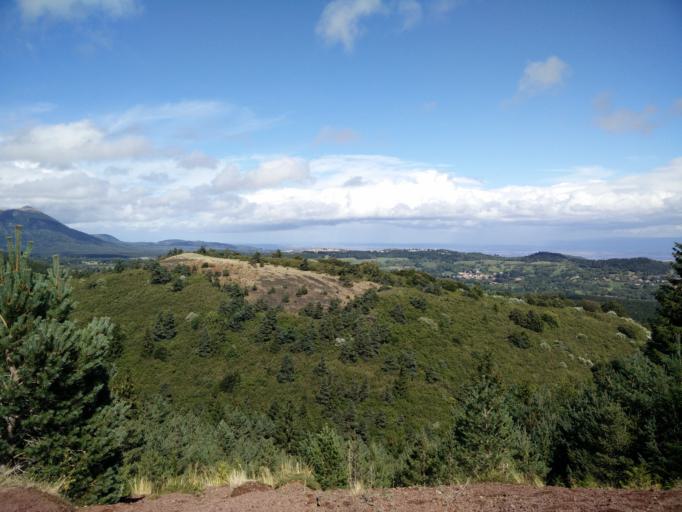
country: FR
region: Auvergne
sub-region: Departement du Puy-de-Dome
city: Aydat
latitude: 45.7066
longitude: 2.9620
